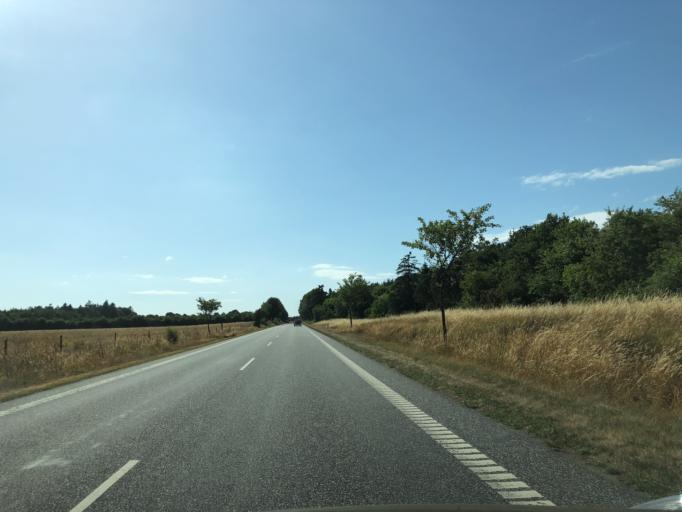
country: DK
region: North Denmark
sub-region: Vesthimmerland Kommune
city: Alestrup
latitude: 56.6119
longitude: 9.3972
